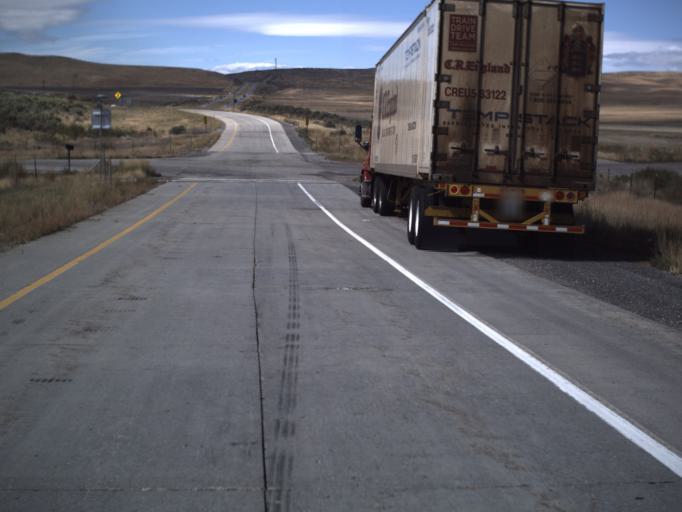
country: US
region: Utah
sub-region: Box Elder County
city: Garland
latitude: 41.8852
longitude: -112.4889
